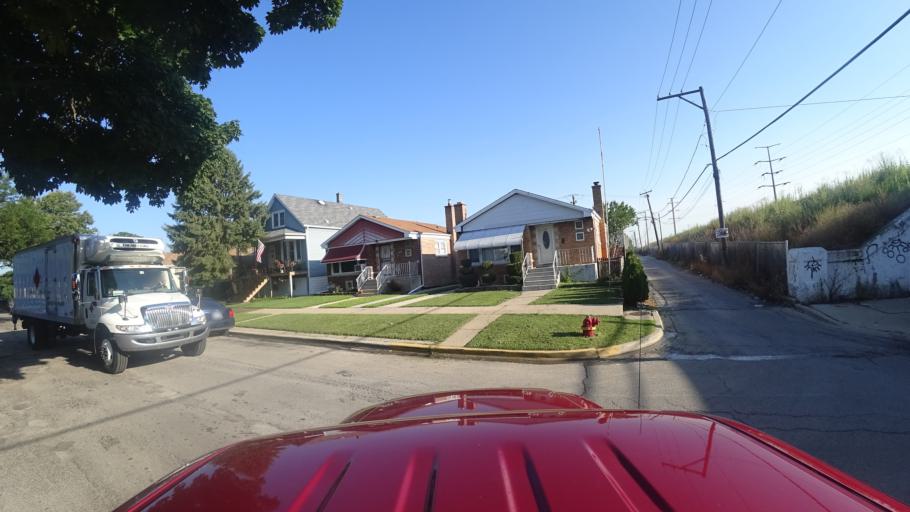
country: US
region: Illinois
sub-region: Cook County
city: Hometown
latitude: 41.7879
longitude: -87.7135
